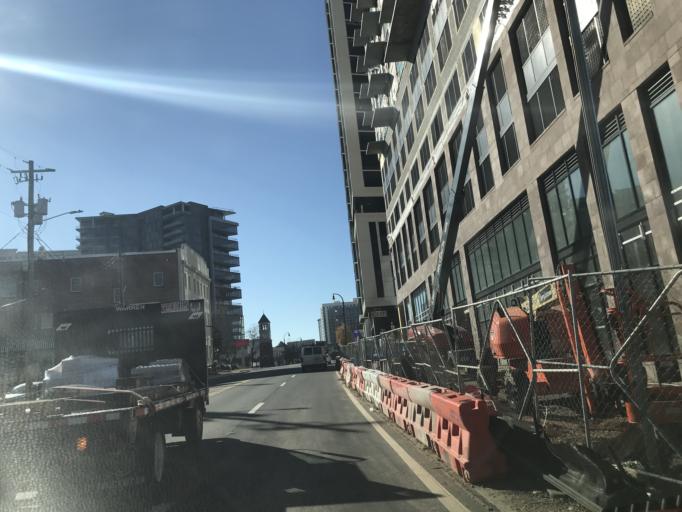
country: US
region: Georgia
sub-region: DeKalb County
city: North Atlanta
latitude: 33.8419
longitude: -84.3790
